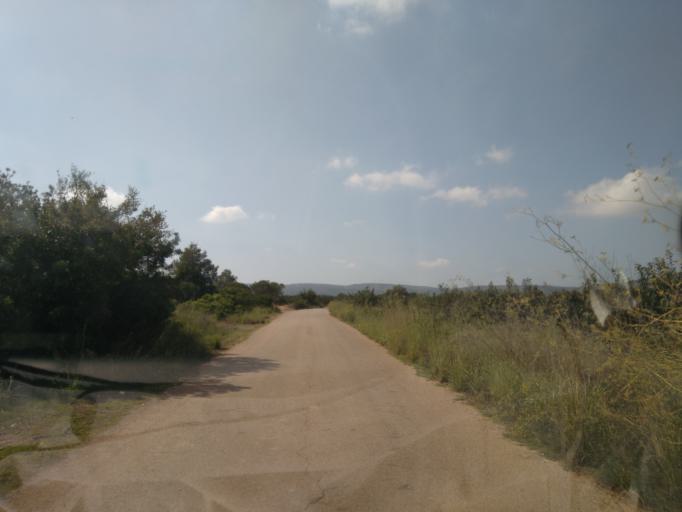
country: ES
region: Valencia
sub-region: Provincia de Valencia
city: Tous
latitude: 39.1701
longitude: -0.5629
